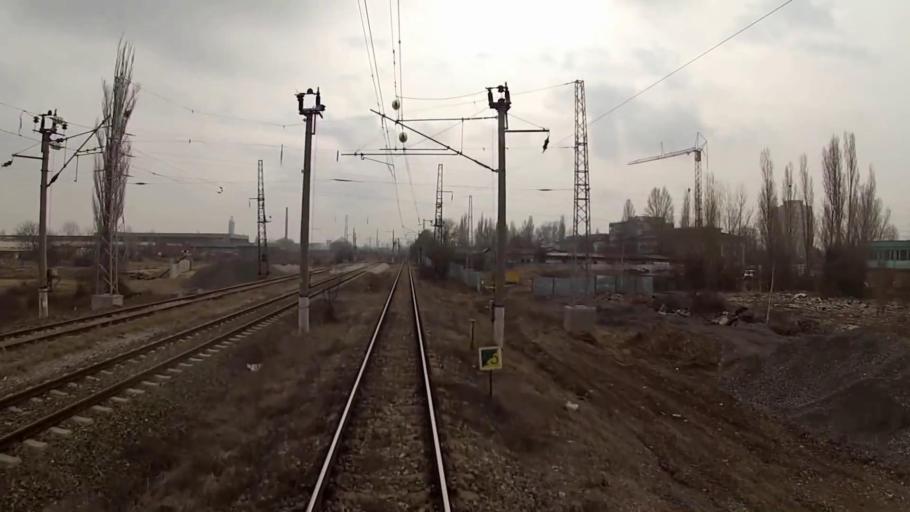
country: BG
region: Sofia-Capital
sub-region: Stolichna Obshtina
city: Sofia
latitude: 42.6627
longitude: 23.4219
